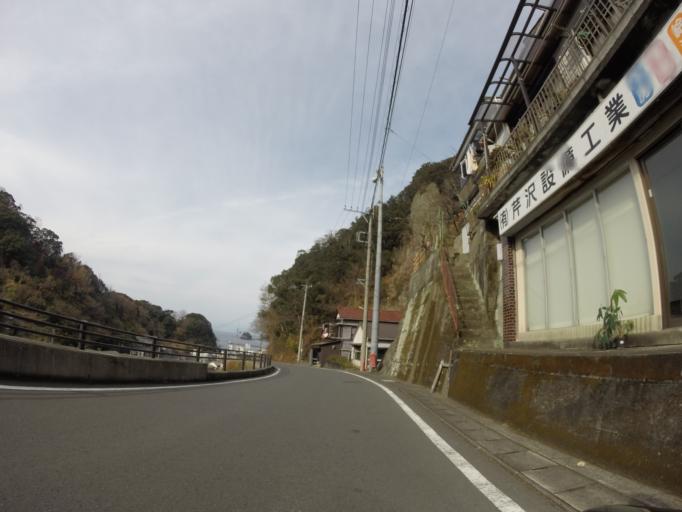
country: JP
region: Shizuoka
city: Heda
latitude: 34.7995
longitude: 138.7654
